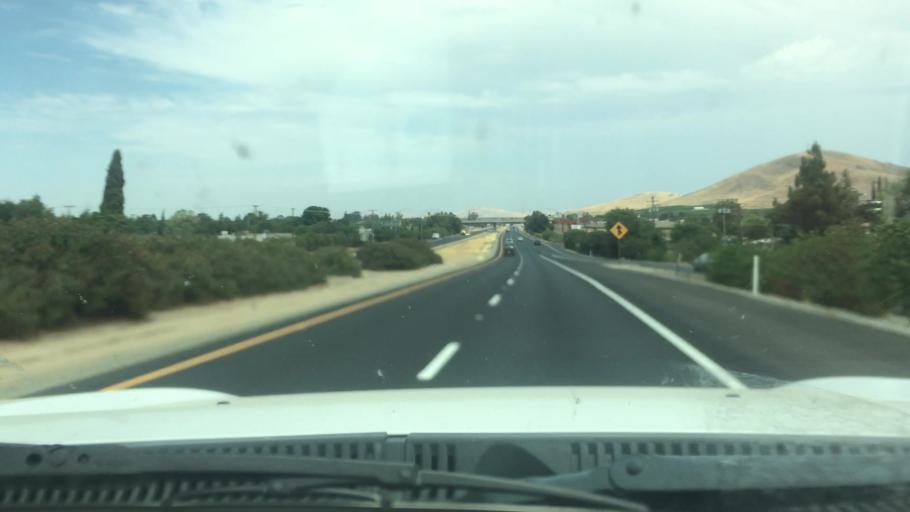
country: US
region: California
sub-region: Tulare County
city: Porterville
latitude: 36.0822
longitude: -119.0391
